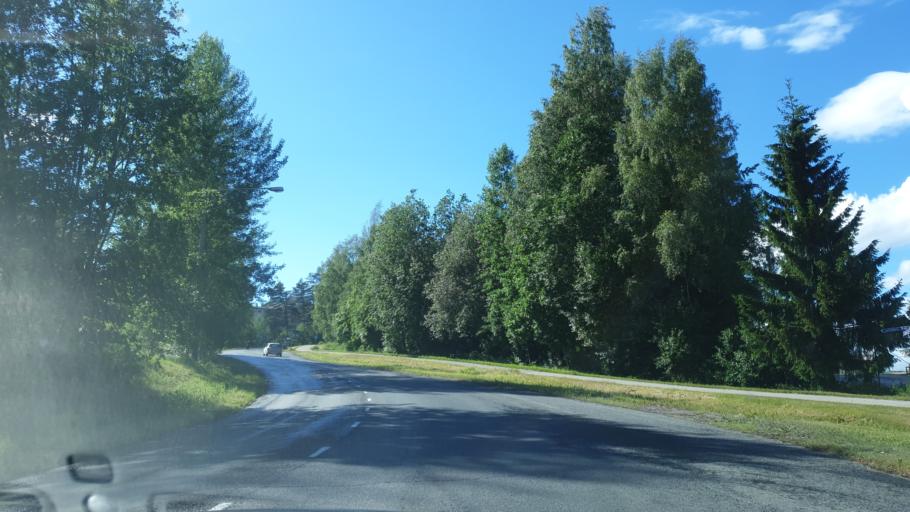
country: FI
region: Northern Savo
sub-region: Kuopio
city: Kuopio
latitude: 62.9058
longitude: 27.6519
